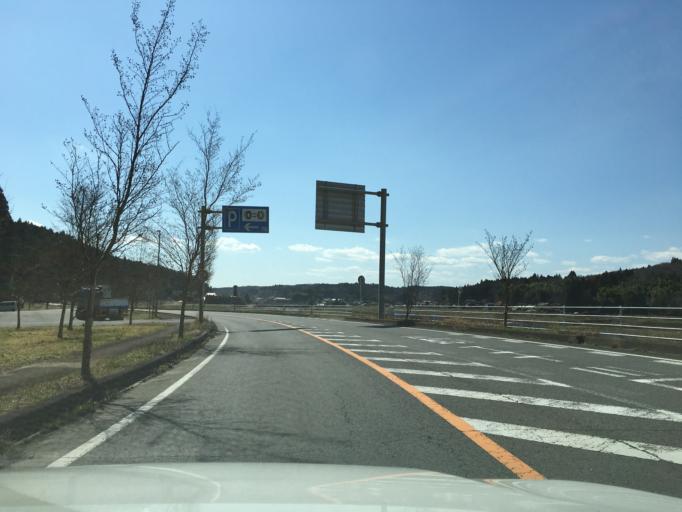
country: JP
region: Tochigi
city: Kuroiso
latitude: 36.9497
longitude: 140.1487
